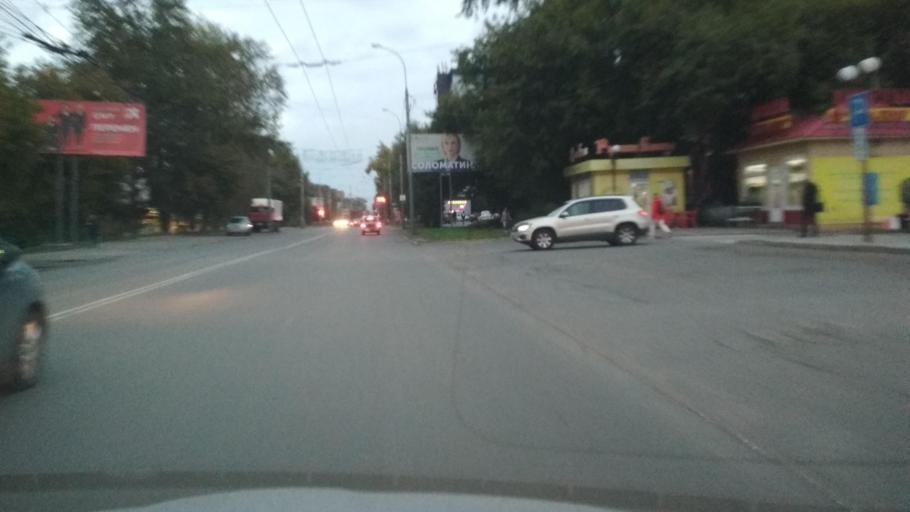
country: RU
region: Tomsk
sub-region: Tomskiy Rayon
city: Tomsk
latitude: 56.4761
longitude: 84.9841
